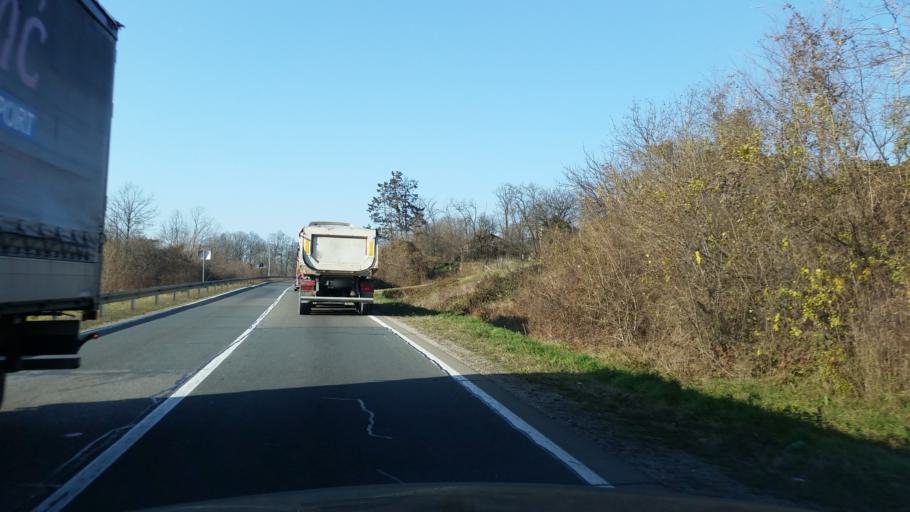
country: RS
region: Central Serbia
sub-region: Kolubarski Okrug
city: Lajkovac
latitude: 44.3478
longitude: 20.1954
